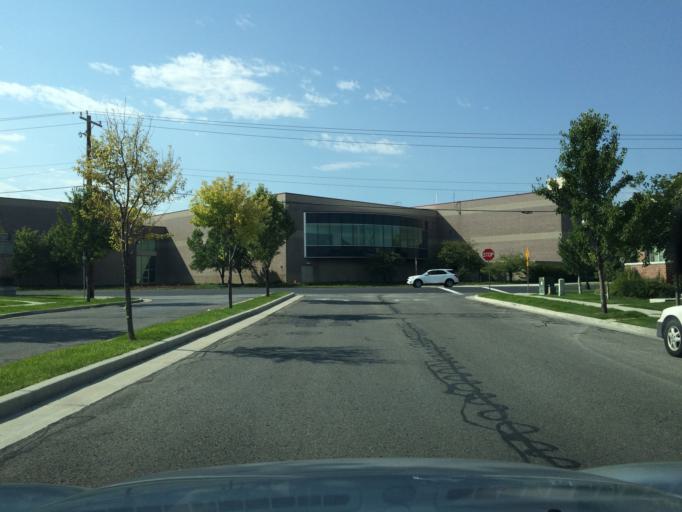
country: US
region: Utah
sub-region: Salt Lake County
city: West Valley City
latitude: 40.7044
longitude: -112.0202
